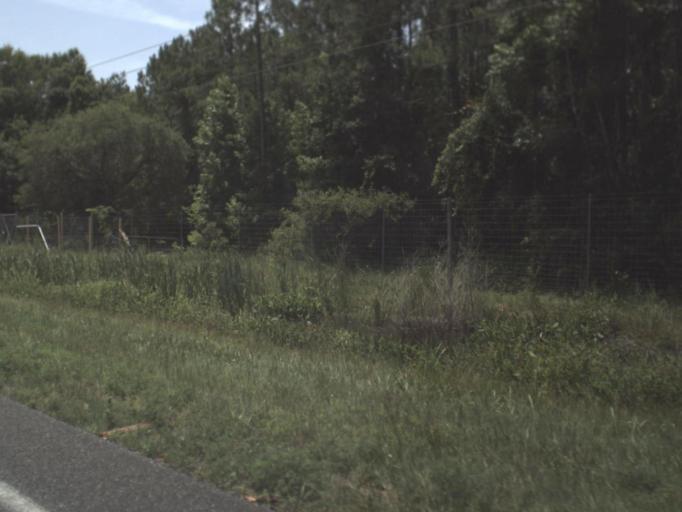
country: US
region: Florida
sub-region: Taylor County
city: Steinhatchee
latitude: 29.8512
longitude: -83.3806
